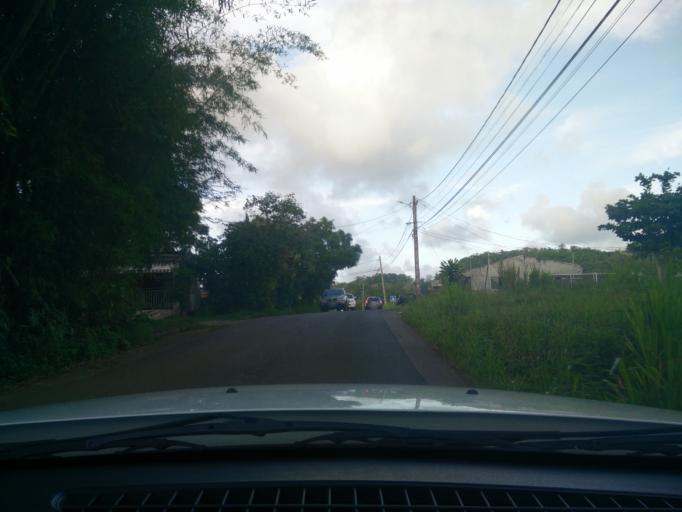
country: GP
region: Guadeloupe
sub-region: Guadeloupe
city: Les Abymes
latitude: 16.2546
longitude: -61.5038
